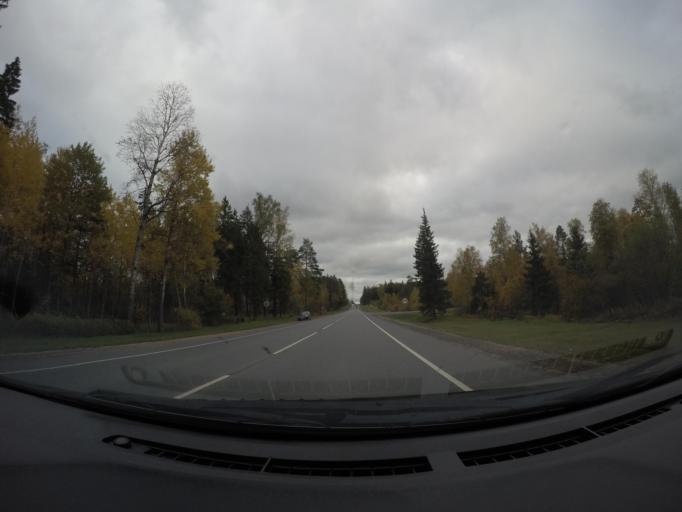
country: RU
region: Moskovskaya
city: Dorokhovo
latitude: 55.6163
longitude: 36.3475
